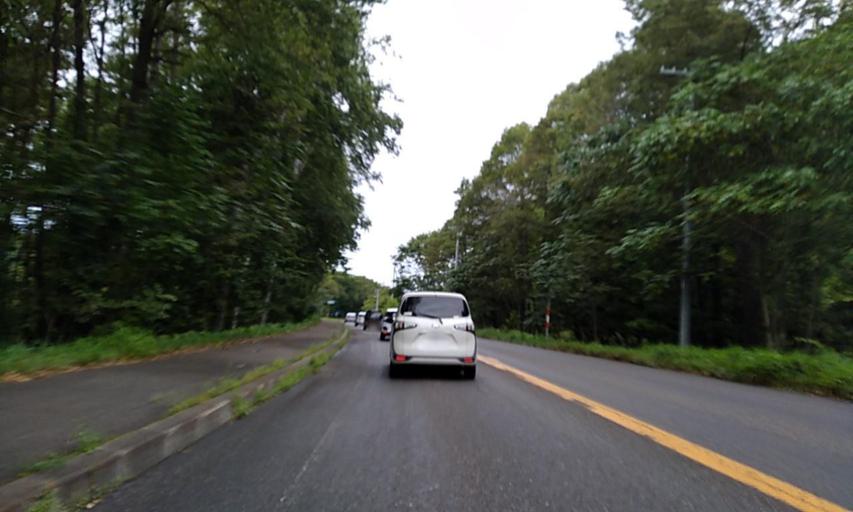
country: JP
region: Hokkaido
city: Abashiri
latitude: 43.9749
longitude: 144.2178
